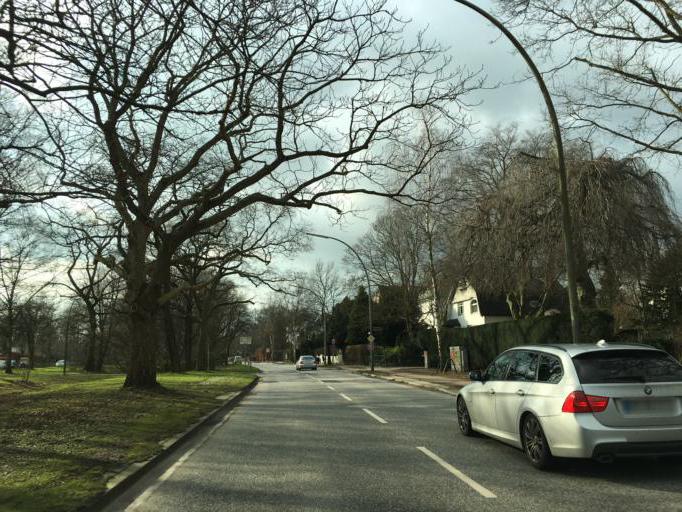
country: DE
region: Hamburg
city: Altona
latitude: 53.5574
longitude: 9.8938
